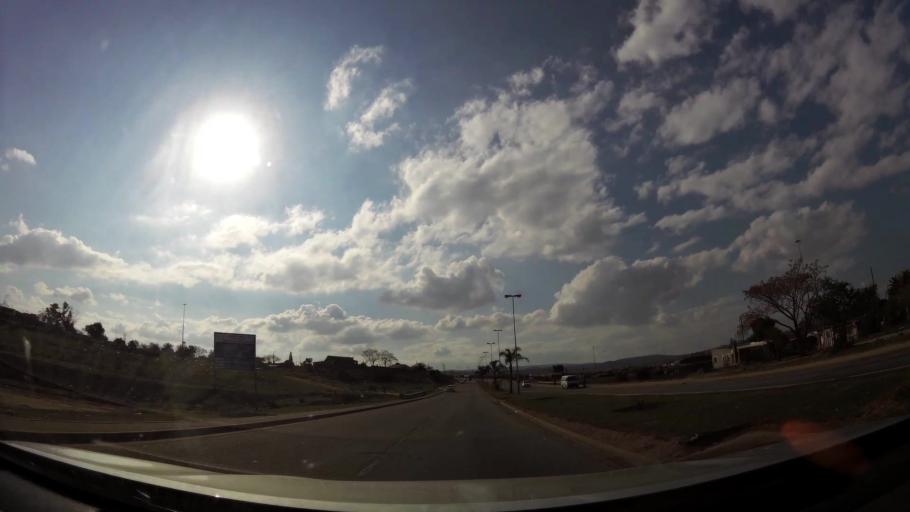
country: ZA
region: Eastern Cape
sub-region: Nelson Mandela Bay Metropolitan Municipality
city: Uitenhage
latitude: -33.7581
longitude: 25.3880
